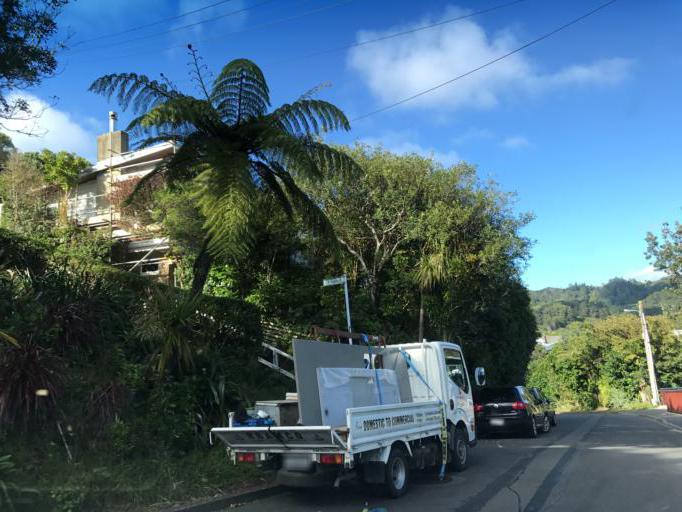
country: NZ
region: Wellington
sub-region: Wellington City
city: Kelburn
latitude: -41.2927
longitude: 174.7452
